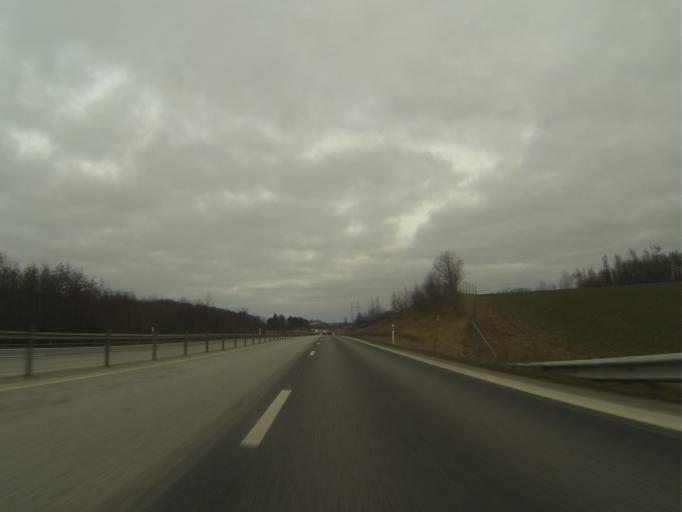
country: SE
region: Skane
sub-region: Skurups Kommun
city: Skurup
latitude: 55.4940
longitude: 13.4518
